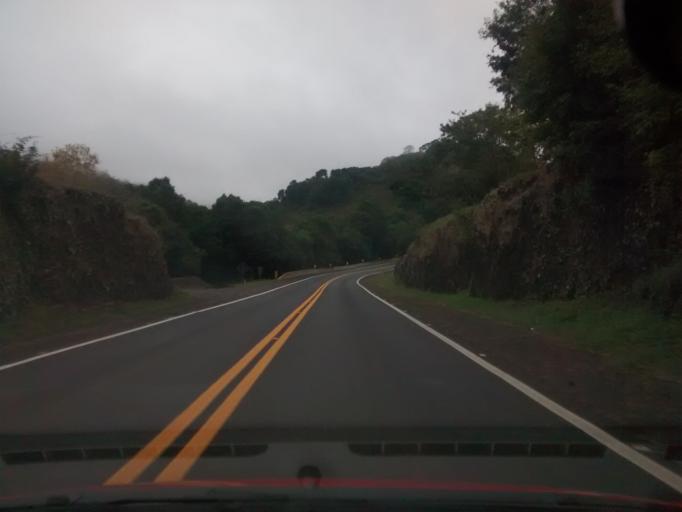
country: BR
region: Rio Grande do Sul
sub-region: Vacaria
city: Estrela
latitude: -28.1956
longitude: -50.7422
